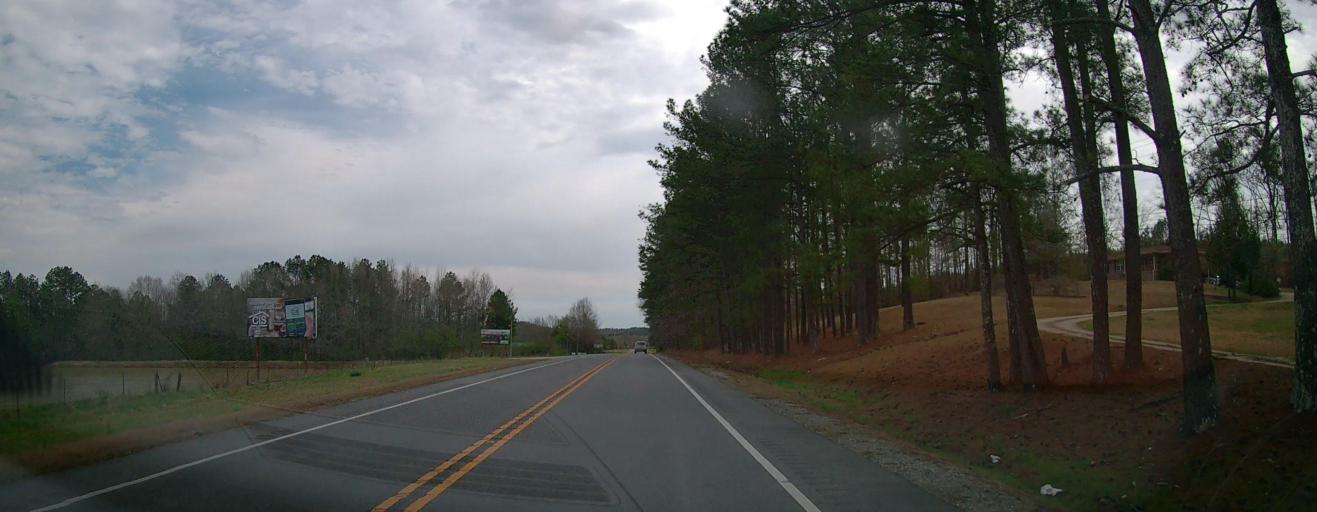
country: US
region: Alabama
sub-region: Marion County
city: Guin
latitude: 34.0118
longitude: -87.9355
